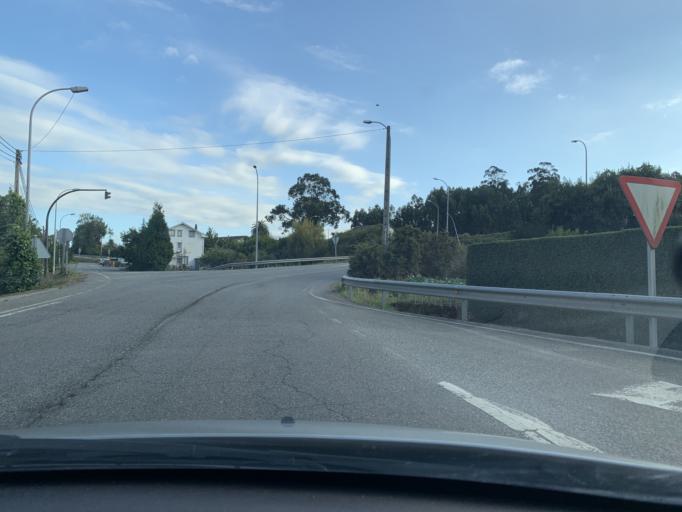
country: ES
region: Galicia
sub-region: Provincia de Lugo
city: Foz
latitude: 43.5630
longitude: -7.2718
